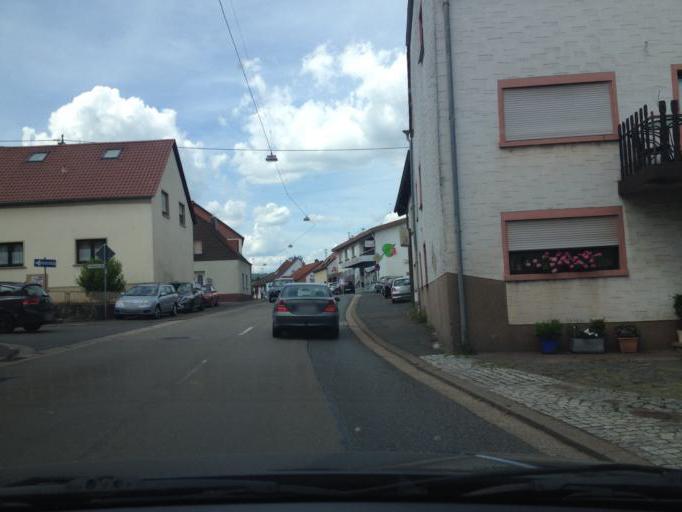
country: DE
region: Saarland
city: Oberthal
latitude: 49.4977
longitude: 7.1096
